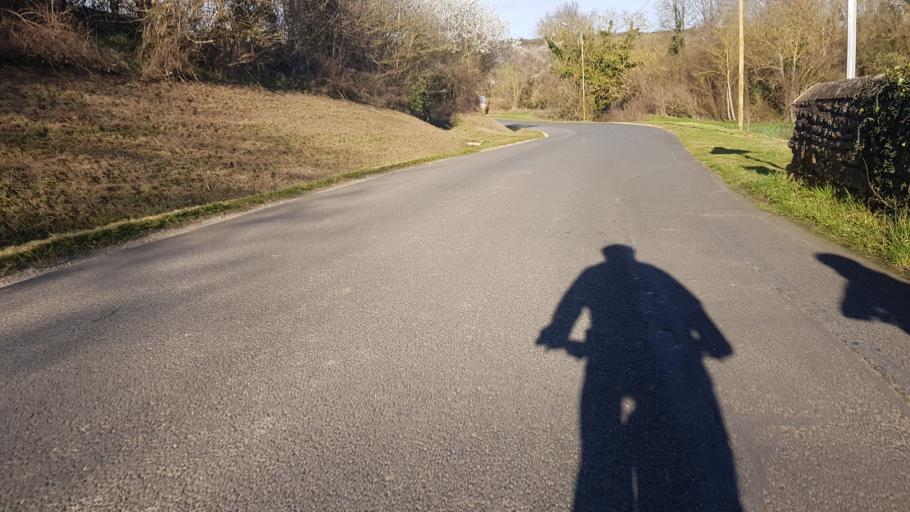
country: FR
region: Poitou-Charentes
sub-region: Departement de la Vienne
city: Migne-Auxances
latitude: 46.6390
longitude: 0.3368
